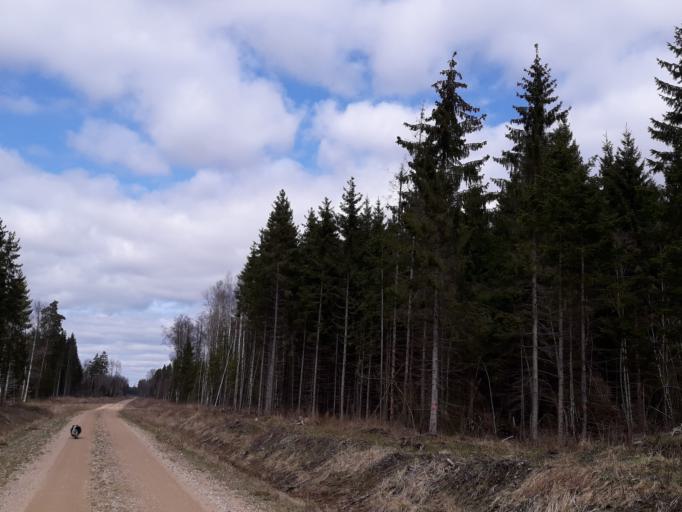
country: LV
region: Talsu Rajons
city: Sabile
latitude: 56.8928
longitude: 22.3804
